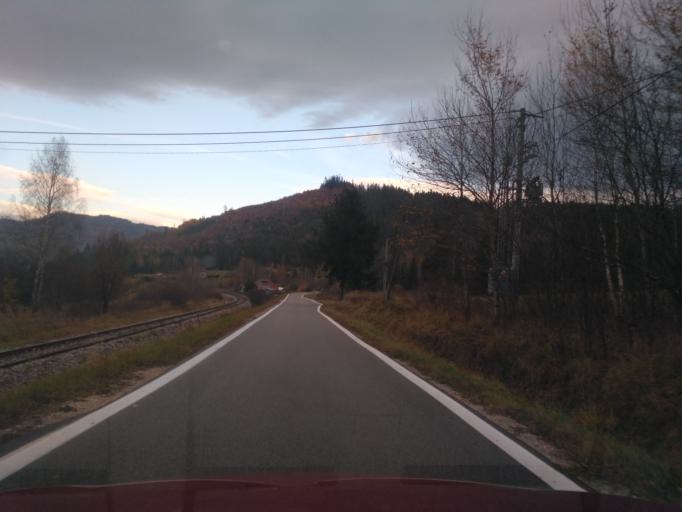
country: SK
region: Kosicky
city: Spisska Nova Ves
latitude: 48.8219
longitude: 20.5978
